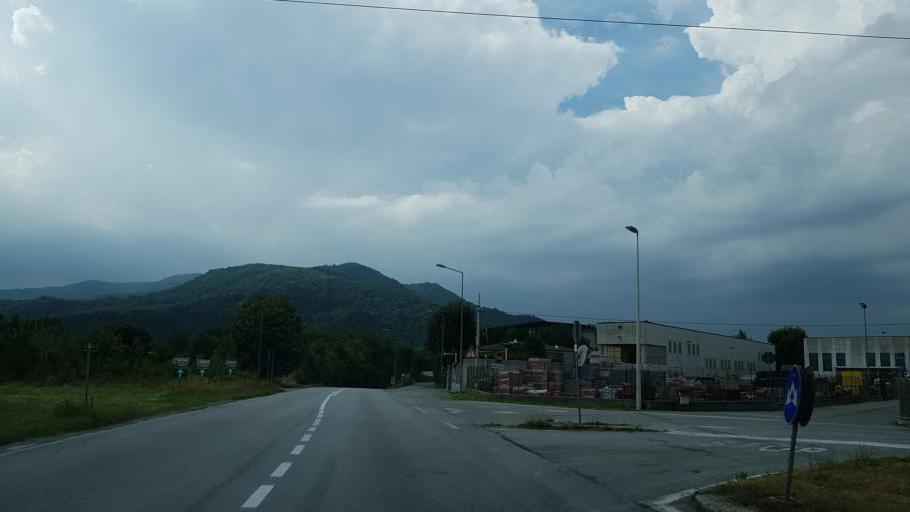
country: IT
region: Piedmont
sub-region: Provincia di Cuneo
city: Borgo San Dalmazzo
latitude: 44.3385
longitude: 7.4778
